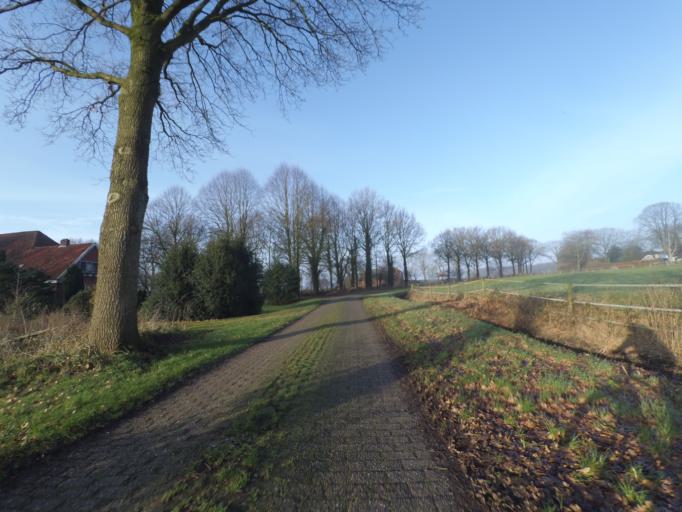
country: NL
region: Drenthe
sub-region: Gemeente Borger-Odoorn
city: Borger
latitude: 52.8998
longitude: 6.7946
